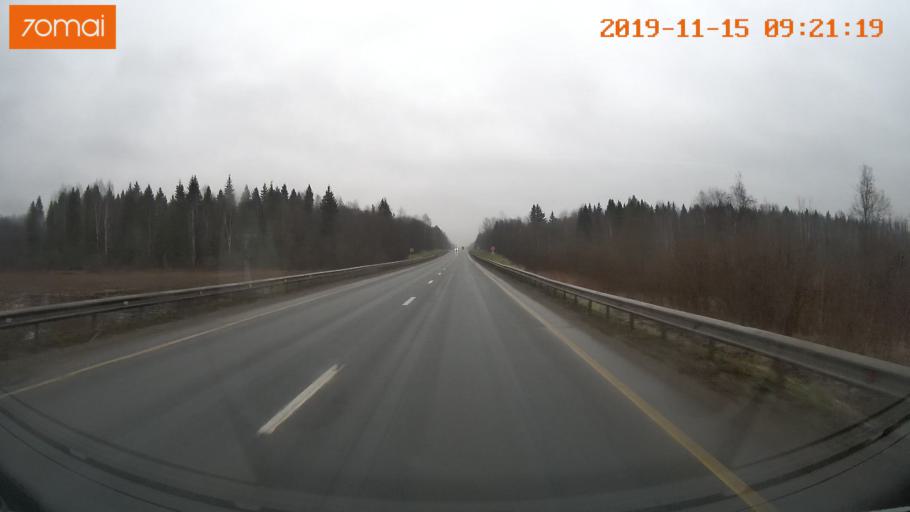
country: RU
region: Vologda
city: Tonshalovo
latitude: 59.2940
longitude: 38.0604
